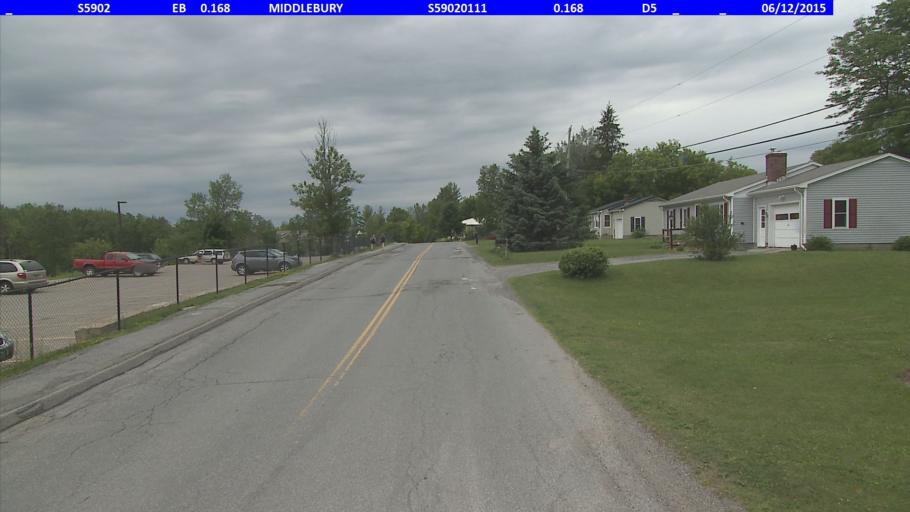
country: US
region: Vermont
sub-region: Addison County
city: Middlebury (village)
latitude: 44.0081
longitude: -73.1632
